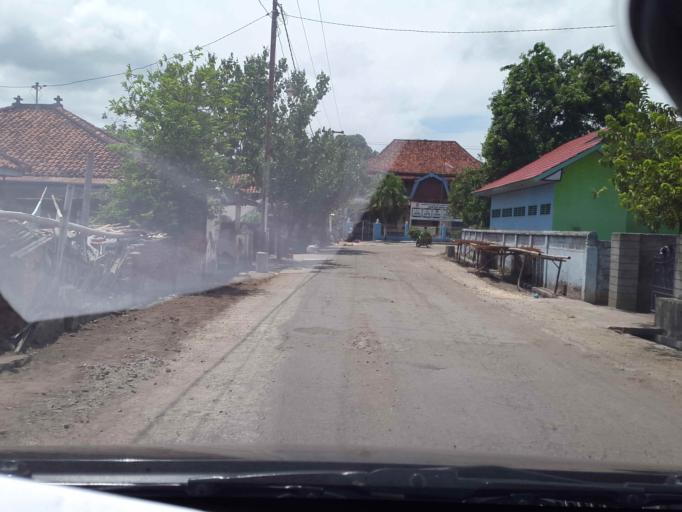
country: ID
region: West Nusa Tenggara
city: Jelateng Timur
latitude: -8.6858
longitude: 116.0954
